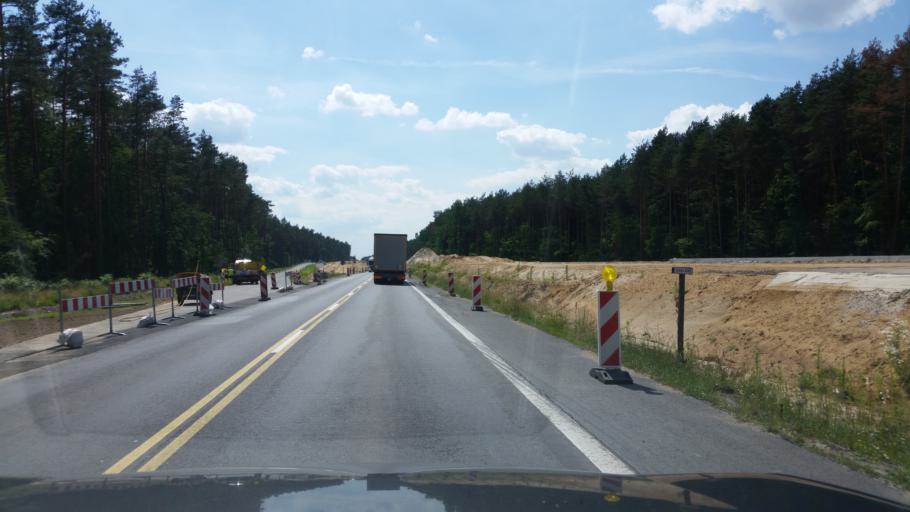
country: PL
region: Masovian Voivodeship
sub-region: Powiat wyszkowski
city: Branszczyk
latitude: 52.6364
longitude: 21.5283
